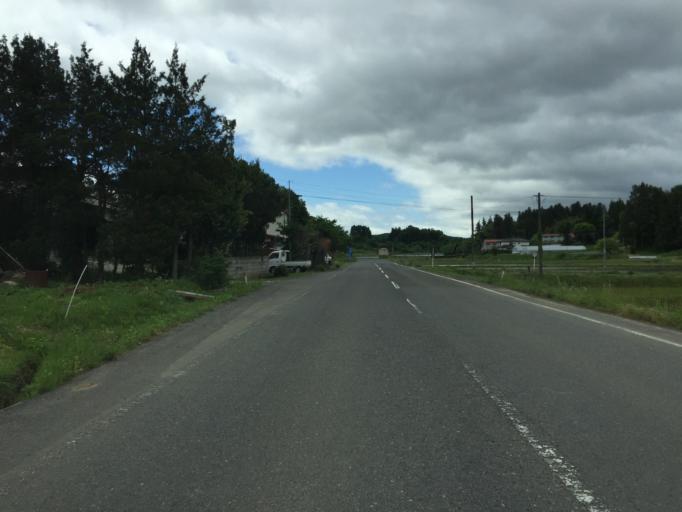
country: JP
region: Fukushima
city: Nihommatsu
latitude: 37.5222
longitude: 140.4736
